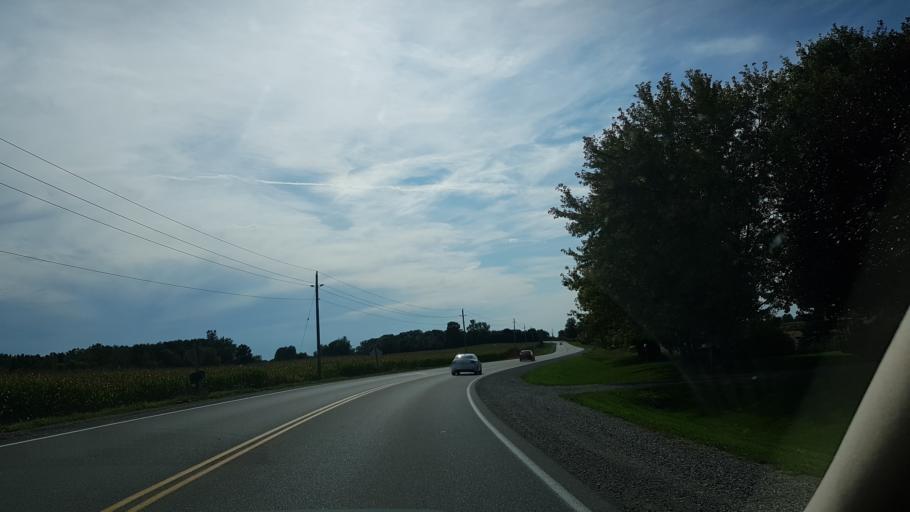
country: CA
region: Ontario
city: Delaware
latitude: 42.9781
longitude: -81.3864
